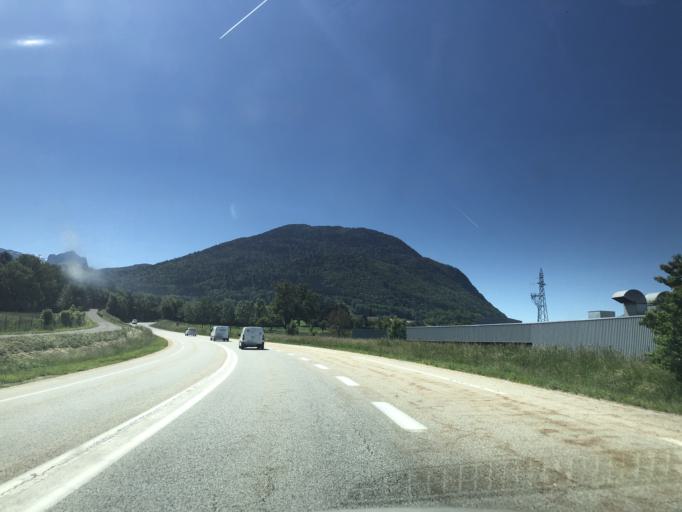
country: FR
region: Rhone-Alpes
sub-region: Departement de la Haute-Savoie
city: Villaz
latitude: 45.9316
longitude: 6.1715
